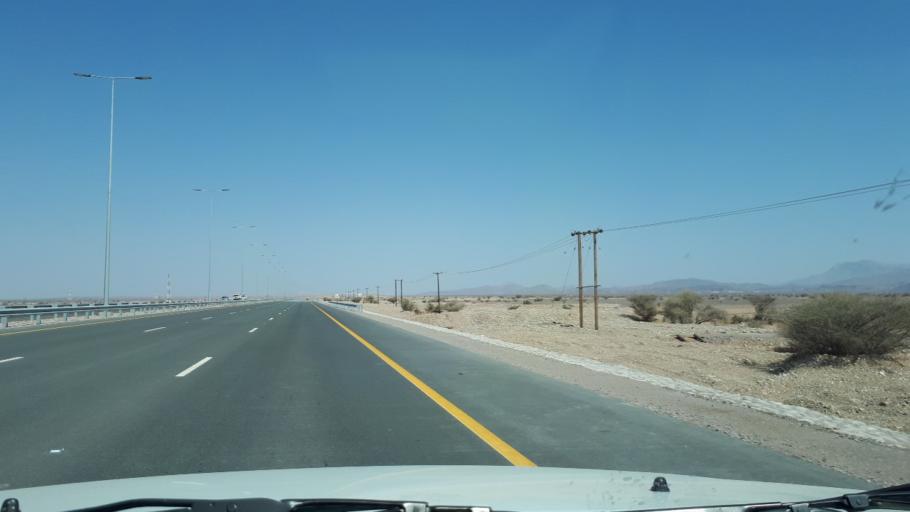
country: OM
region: Ash Sharqiyah
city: Badiyah
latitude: 22.3886
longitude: 59.0818
